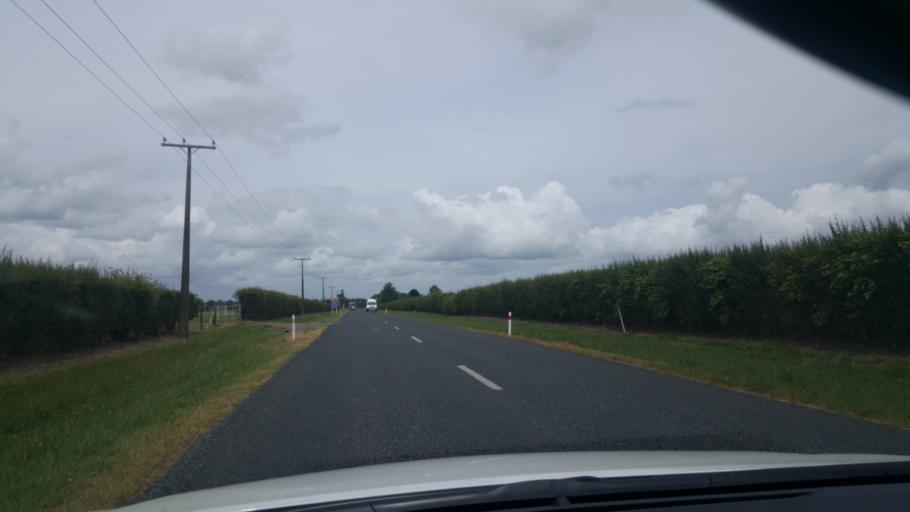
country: NZ
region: Waikato
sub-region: Matamata-Piako District
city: Matamata
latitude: -37.8793
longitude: 175.7293
